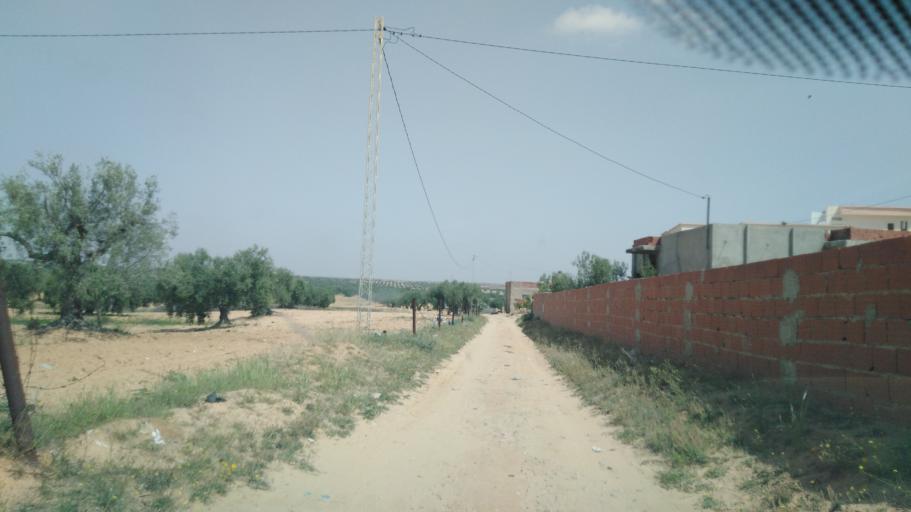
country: TN
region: Safaqis
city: Sfax
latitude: 34.7302
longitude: 10.5745
